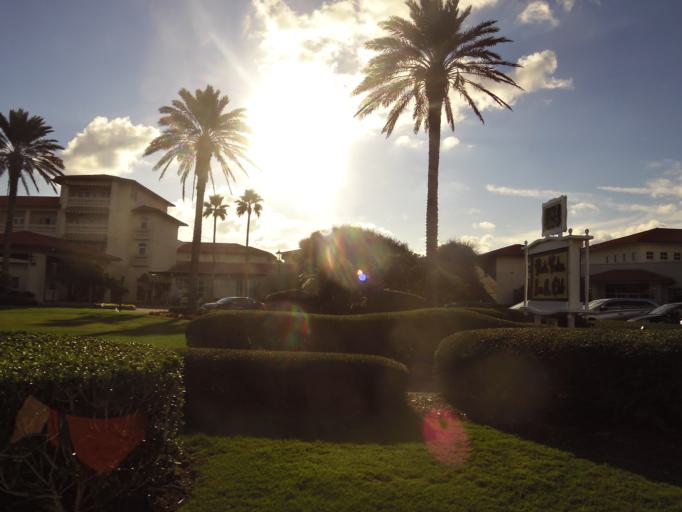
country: US
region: Florida
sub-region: Saint Johns County
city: Ponte Vedra Beach
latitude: 30.2425
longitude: -81.3789
